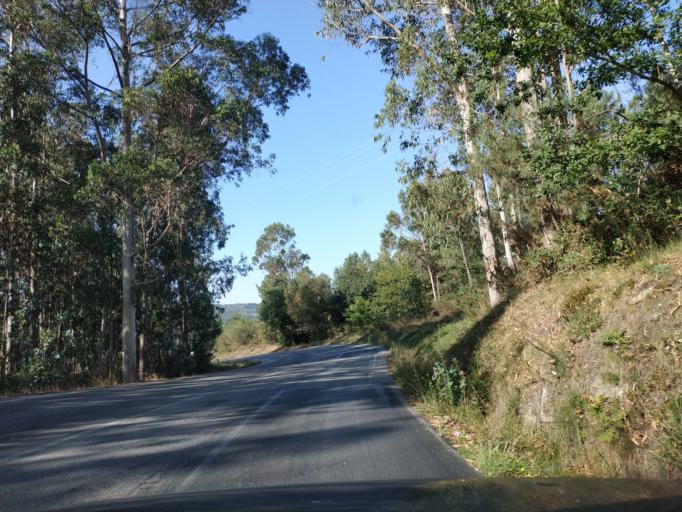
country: ES
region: Galicia
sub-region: Provincia da Coruna
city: Cerceda
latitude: 43.2334
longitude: -8.4647
